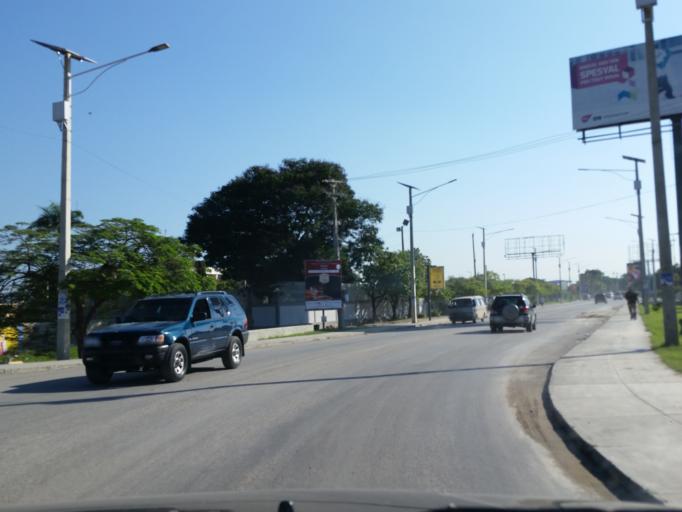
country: HT
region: Ouest
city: Delmas 73
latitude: 18.5749
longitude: -72.3004
